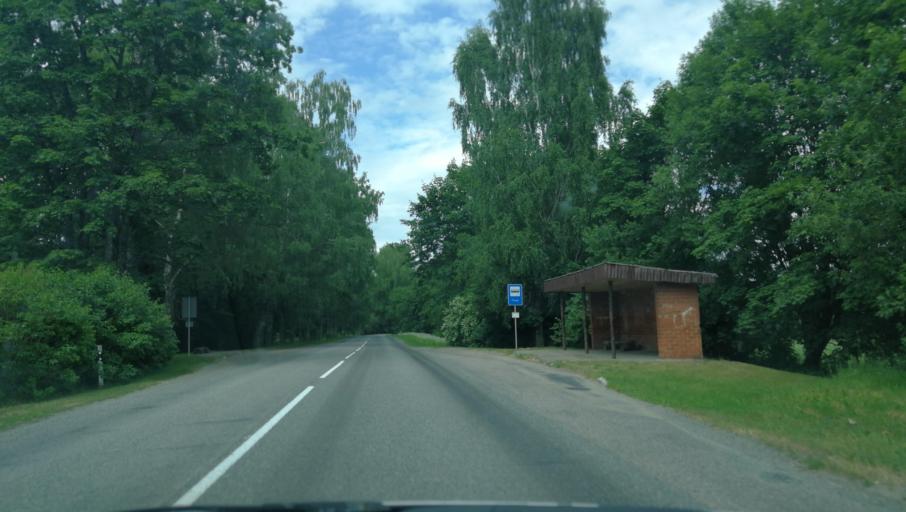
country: LV
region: Rujienas
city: Rujiena
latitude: 57.8568
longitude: 25.3759
